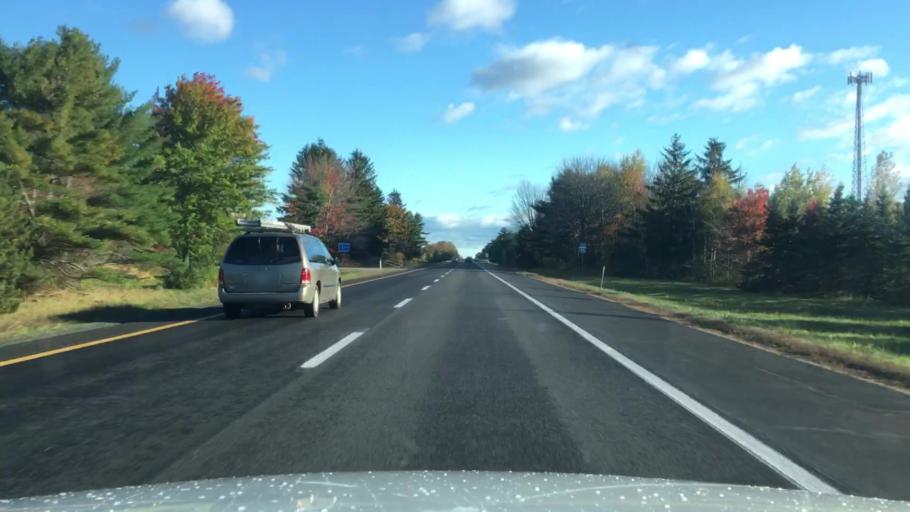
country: US
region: Maine
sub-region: Penobscot County
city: Veazie
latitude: 44.8362
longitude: -68.7381
